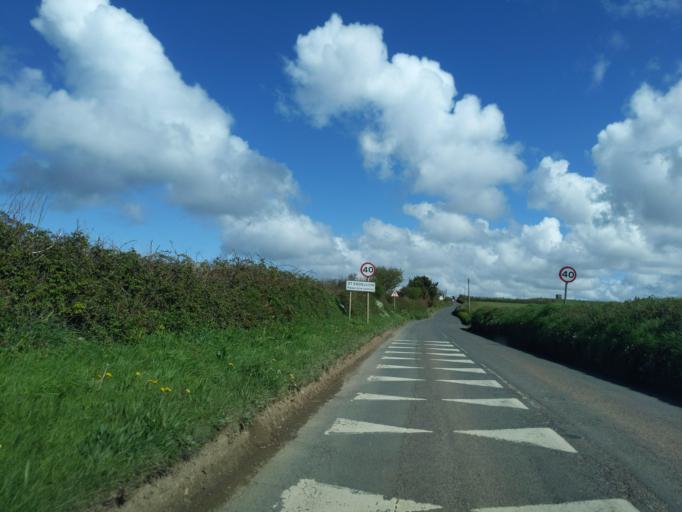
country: GB
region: England
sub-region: Cornwall
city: Wadebridge
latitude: 50.5738
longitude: -4.8395
